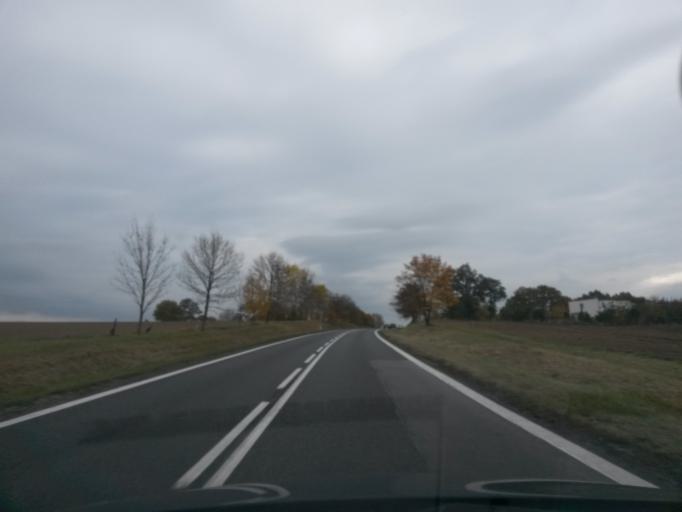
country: PL
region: Lower Silesian Voivodeship
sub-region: Powiat dzierzoniowski
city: Niemcza
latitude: 50.7275
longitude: 16.8290
